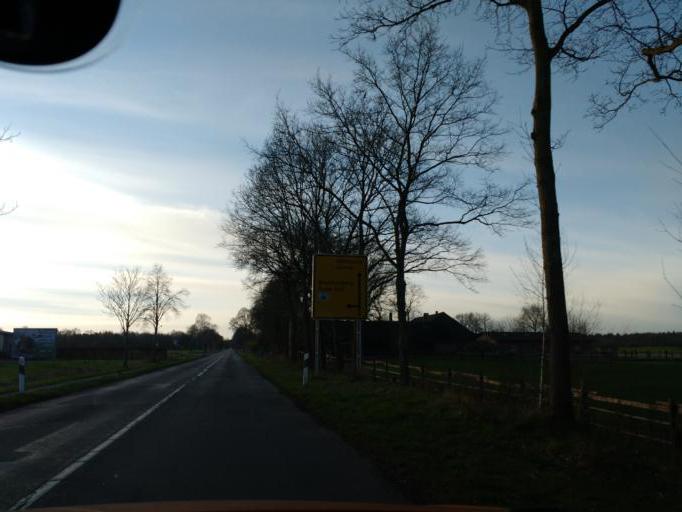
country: DE
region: Lower Saxony
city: Hude
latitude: 53.1121
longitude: 8.4412
